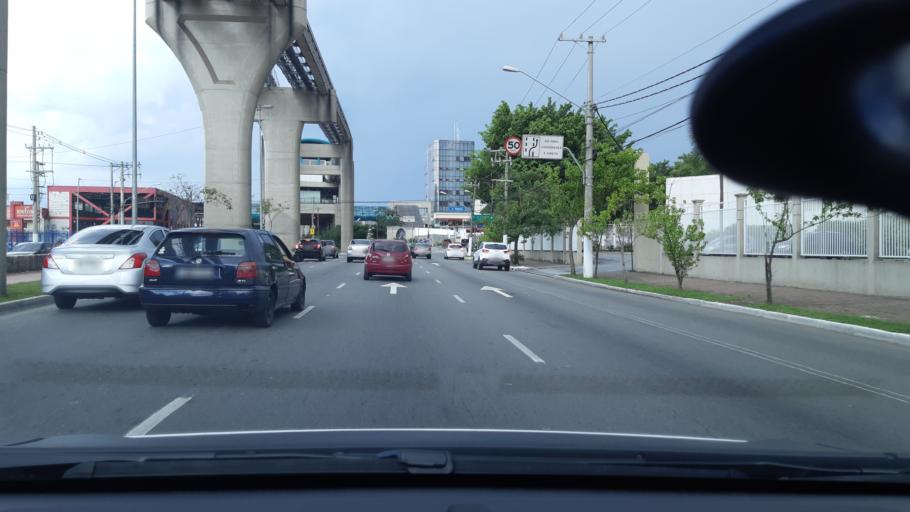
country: BR
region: Sao Paulo
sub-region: Sao Caetano Do Sul
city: Sao Caetano do Sul
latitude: -23.5826
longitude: -46.5639
